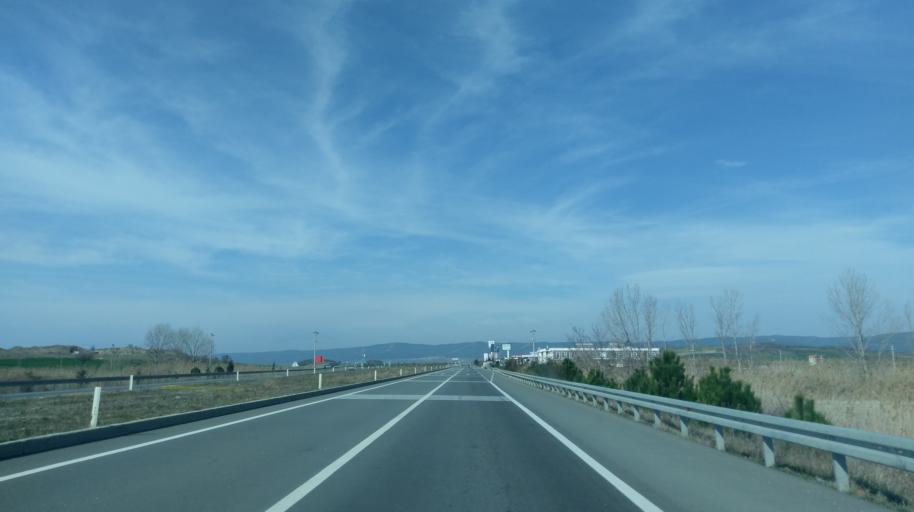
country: TR
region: Canakkale
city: Evrese
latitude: 40.6382
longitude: 26.8626
